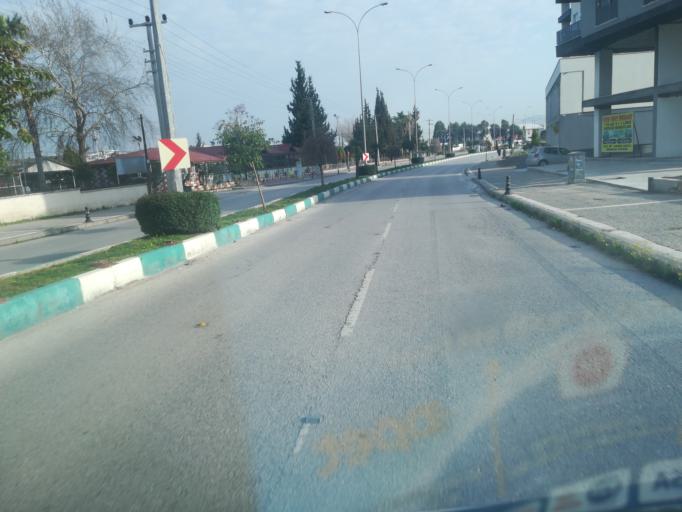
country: TR
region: Osmaniye
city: Osmaniye
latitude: 37.0486
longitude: 36.2274
